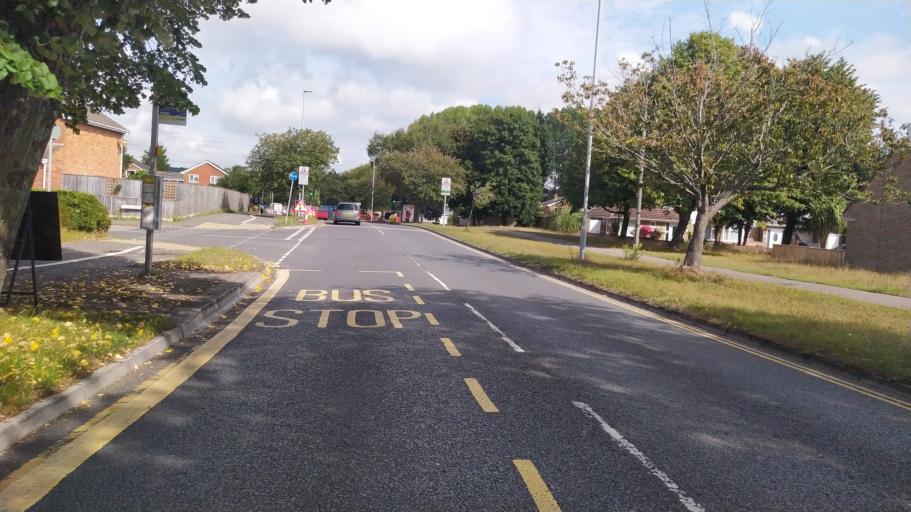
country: GB
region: England
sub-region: Poole
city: Canford Heath
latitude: 50.7462
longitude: -1.9628
